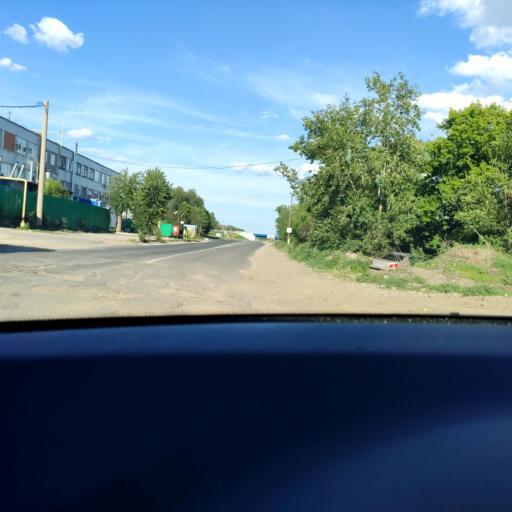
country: RU
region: Samara
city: Smyshlyayevka
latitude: 53.1819
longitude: 50.2967
